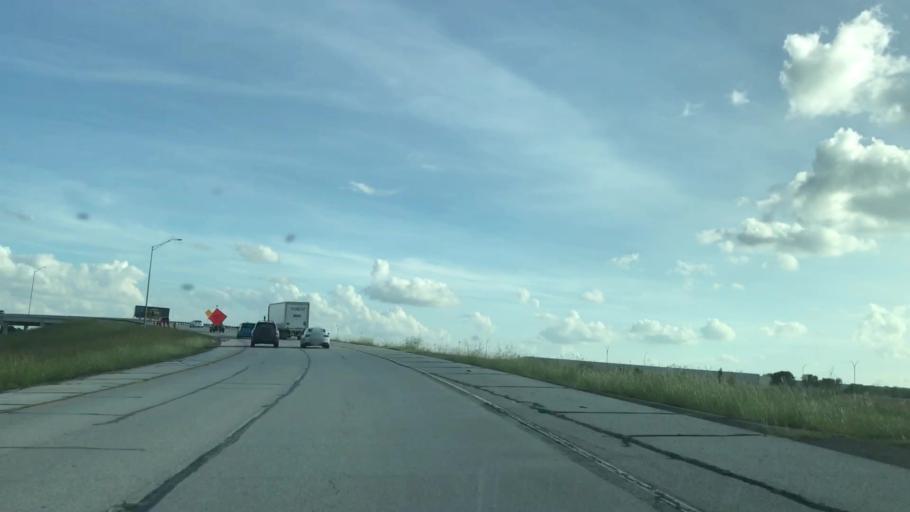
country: US
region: Texas
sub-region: Tarrant County
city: Euless
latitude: 32.8396
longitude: -97.0421
